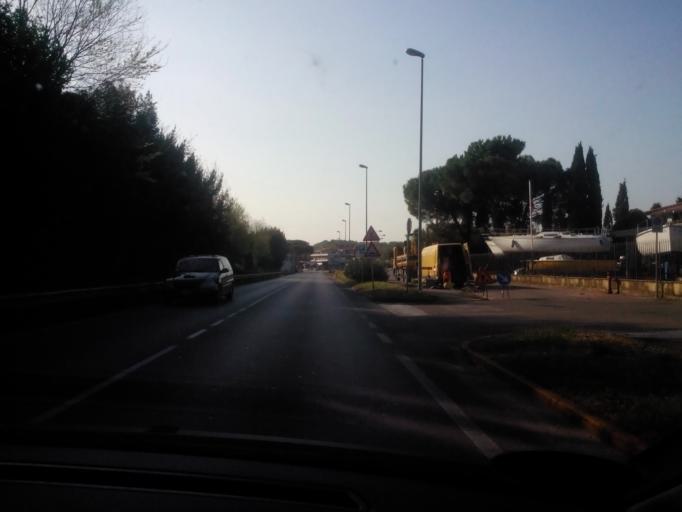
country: IT
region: Lombardy
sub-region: Provincia di Brescia
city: Padenghe sul Garda
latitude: 45.4941
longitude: 10.5116
